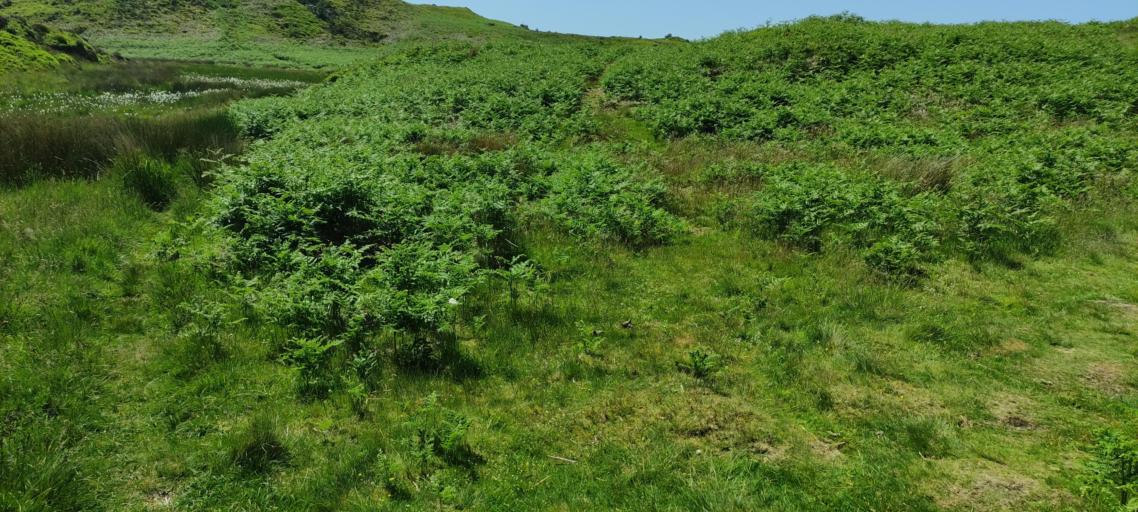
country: GB
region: England
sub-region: Cumbria
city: Seascale
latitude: 54.3782
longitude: -3.3541
